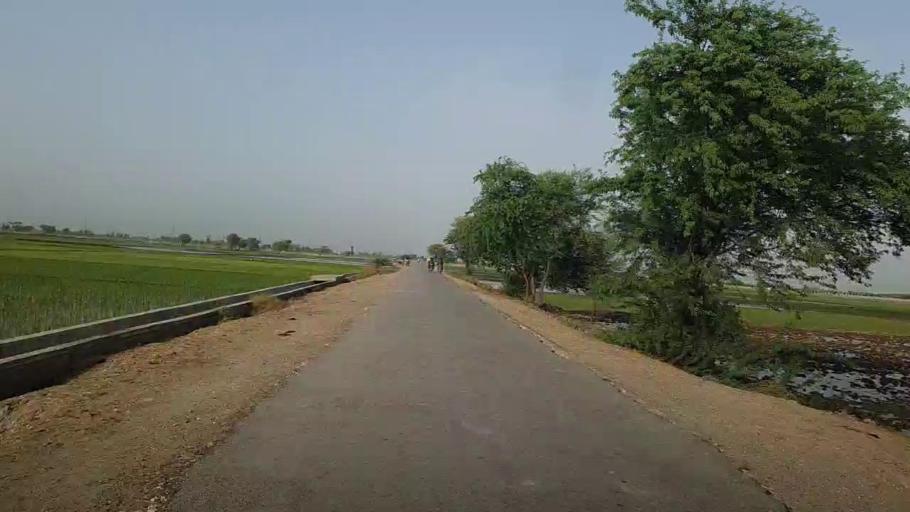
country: PK
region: Sindh
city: Mehar
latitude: 27.1659
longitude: 67.8150
